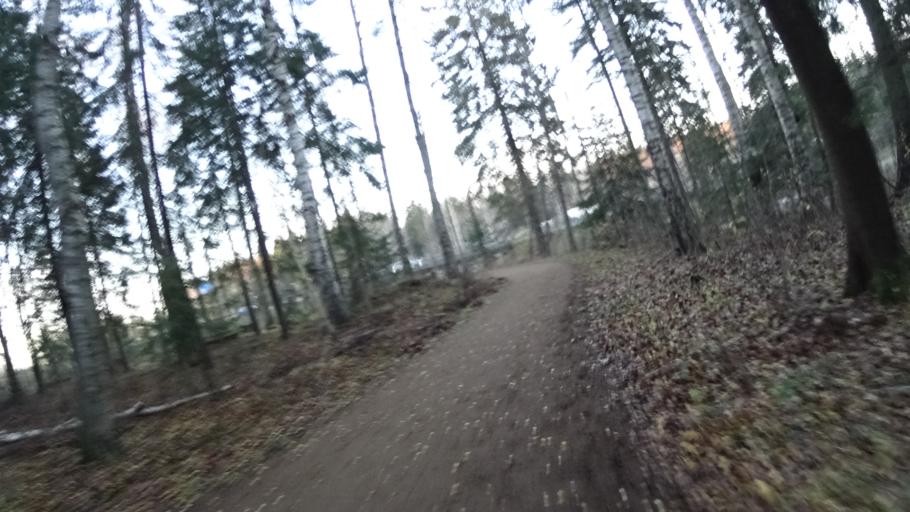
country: FI
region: Uusimaa
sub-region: Helsinki
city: Helsinki
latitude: 60.2356
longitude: 24.9050
